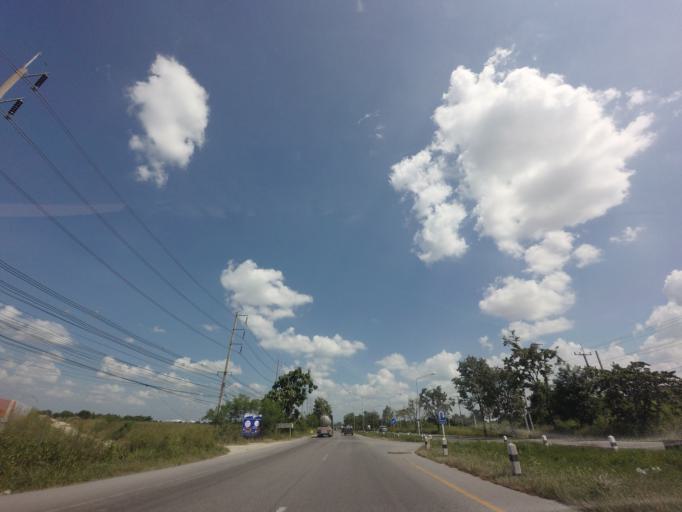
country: TH
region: Chon Buri
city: Ban Bueng
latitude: 13.3004
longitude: 101.1483
